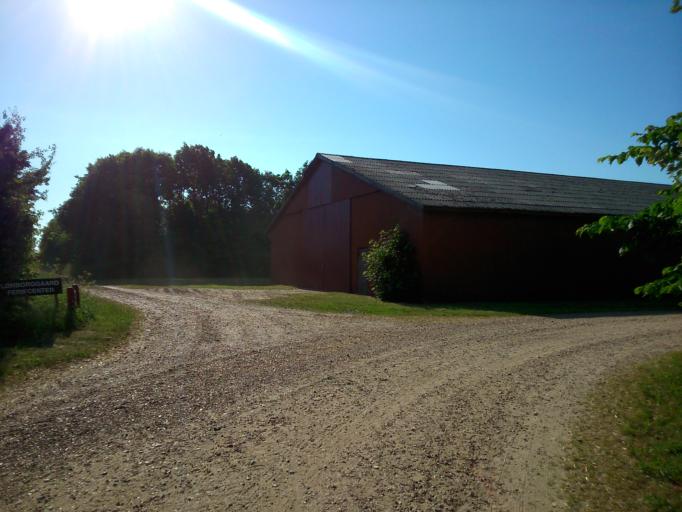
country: DK
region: Central Jutland
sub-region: Ringkobing-Skjern Kommune
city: Skjern
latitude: 55.9016
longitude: 8.4153
